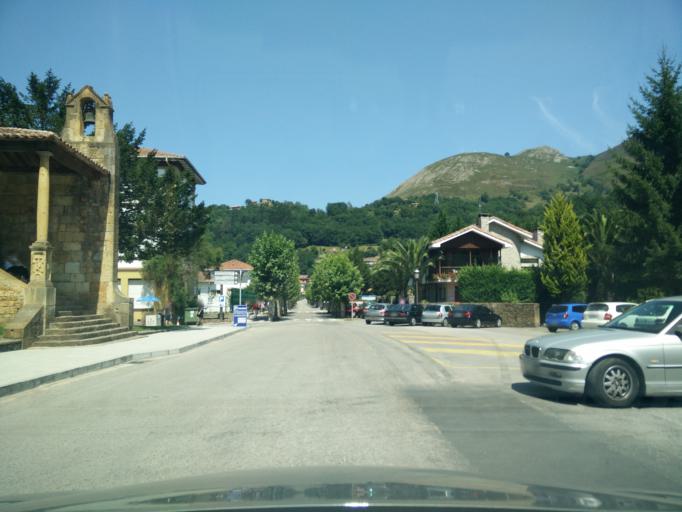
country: ES
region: Asturias
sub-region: Province of Asturias
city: Cangas de Onis
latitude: 43.3526
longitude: -5.1302
